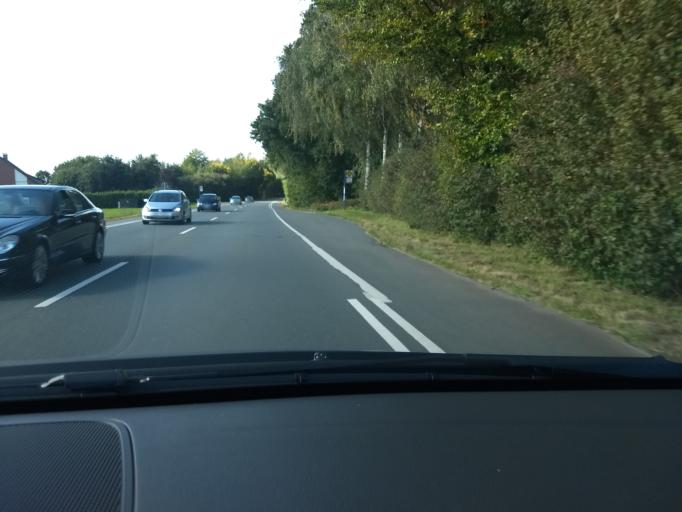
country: DE
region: North Rhine-Westphalia
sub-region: Regierungsbezirk Munster
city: Heiden
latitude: 51.8249
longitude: 6.9100
